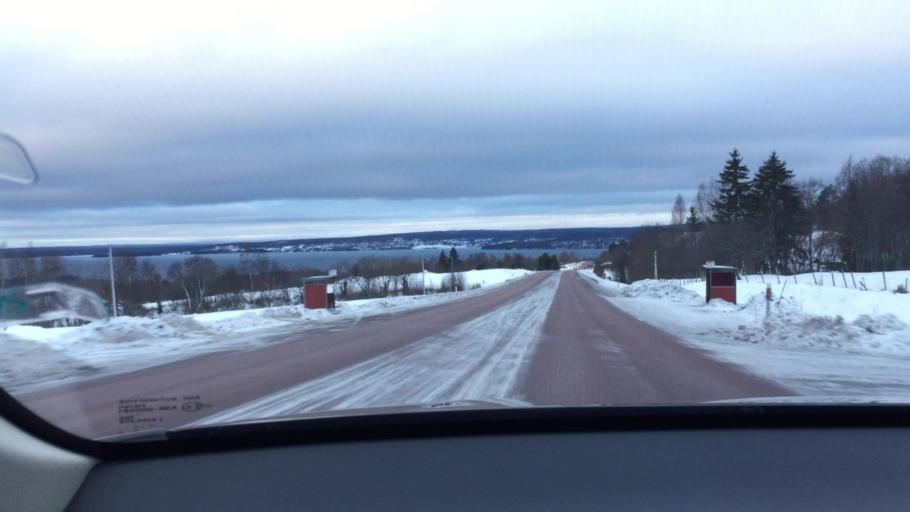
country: SE
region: Dalarna
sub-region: Rattviks Kommun
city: Raettvik
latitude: 60.8476
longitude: 15.1169
